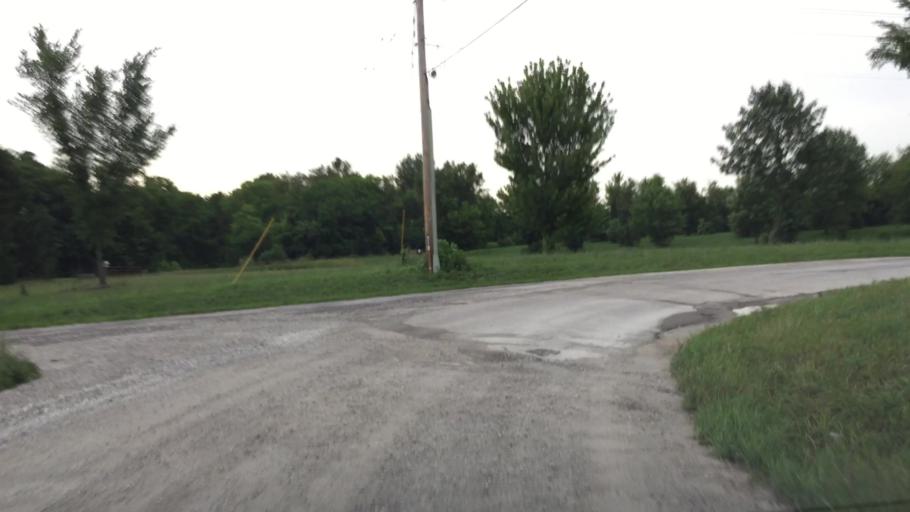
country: US
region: Illinois
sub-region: Hancock County
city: Hamilton
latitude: 40.3755
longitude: -91.3613
